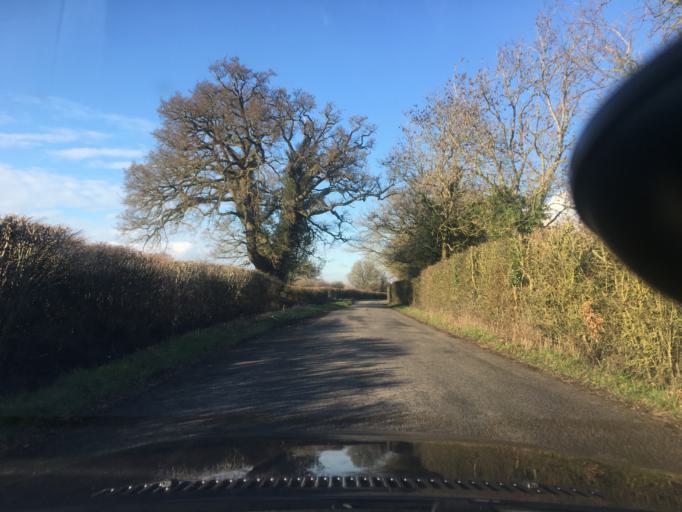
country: GB
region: England
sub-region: West Berkshire
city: Stratfield Mortimer
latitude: 51.3904
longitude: -1.0206
